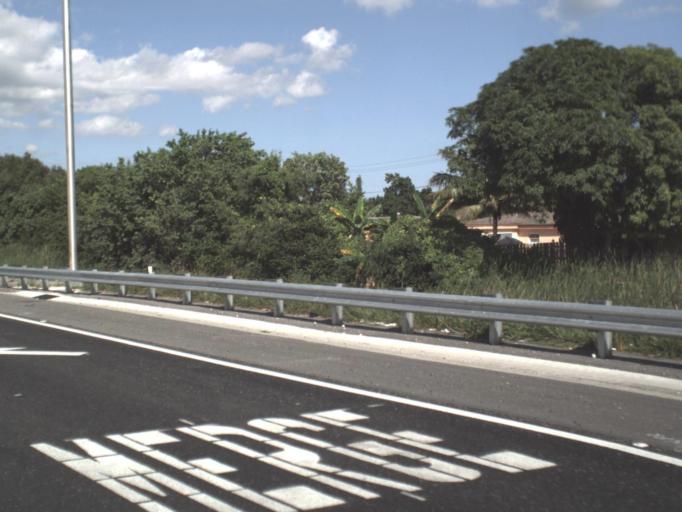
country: US
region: Florida
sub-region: Broward County
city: Miramar
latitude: 25.9849
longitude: -80.2296
